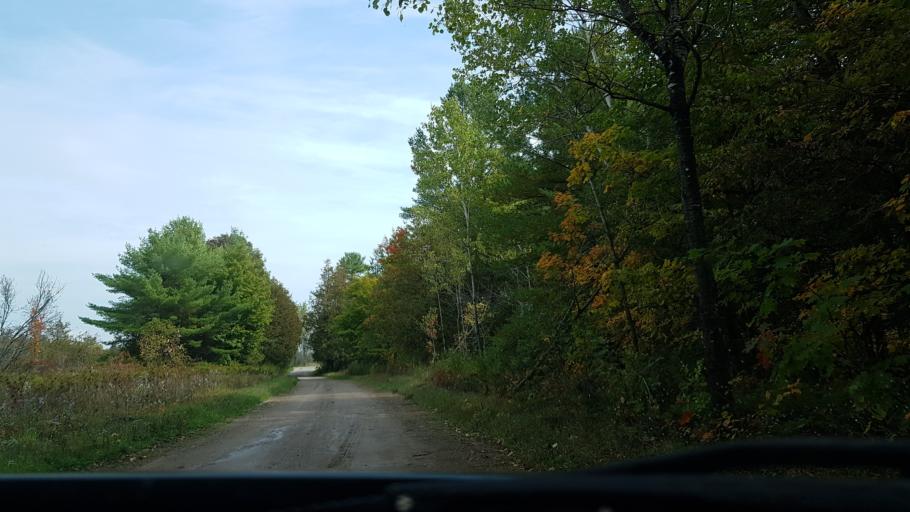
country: CA
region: Ontario
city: Orillia
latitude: 44.6883
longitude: -79.0383
